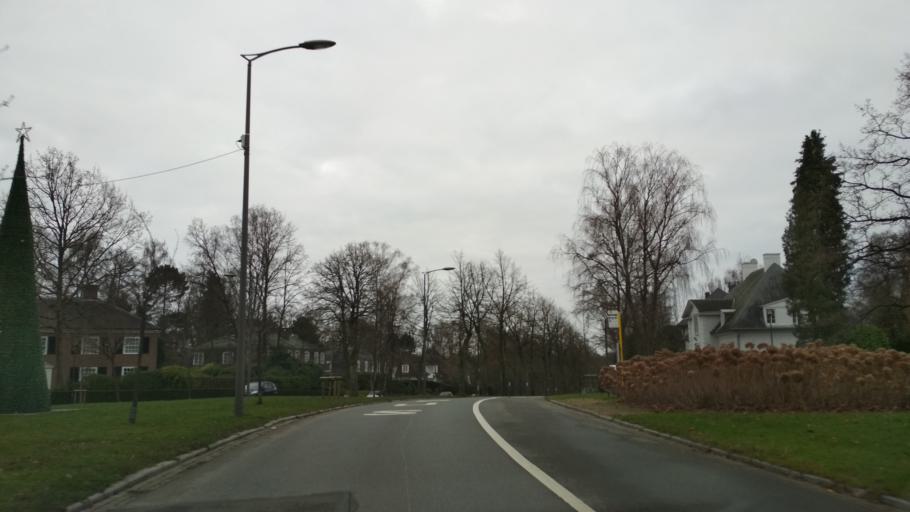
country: BE
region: Flanders
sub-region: Provincie Vlaams-Brabant
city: Wezembeek-Oppem
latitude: 50.8311
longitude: 4.4716
